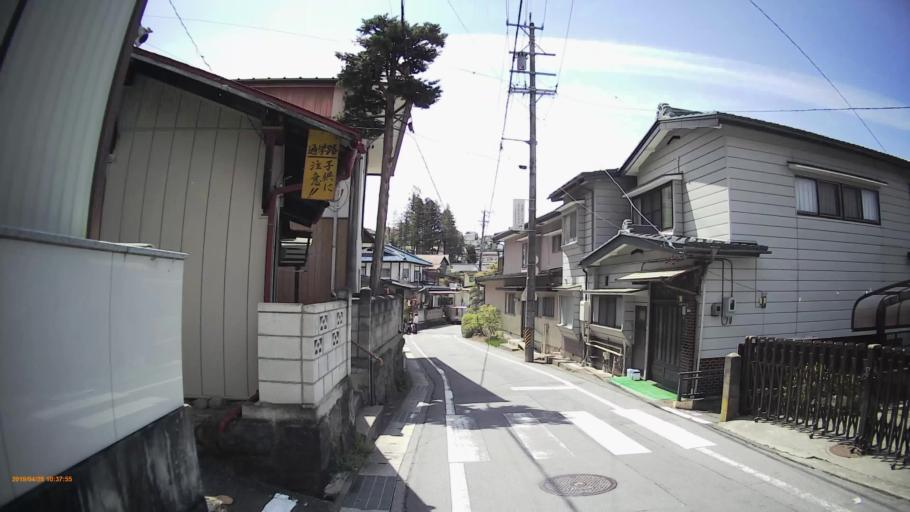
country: JP
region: Nagano
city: Suwa
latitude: 36.0529
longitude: 138.1186
